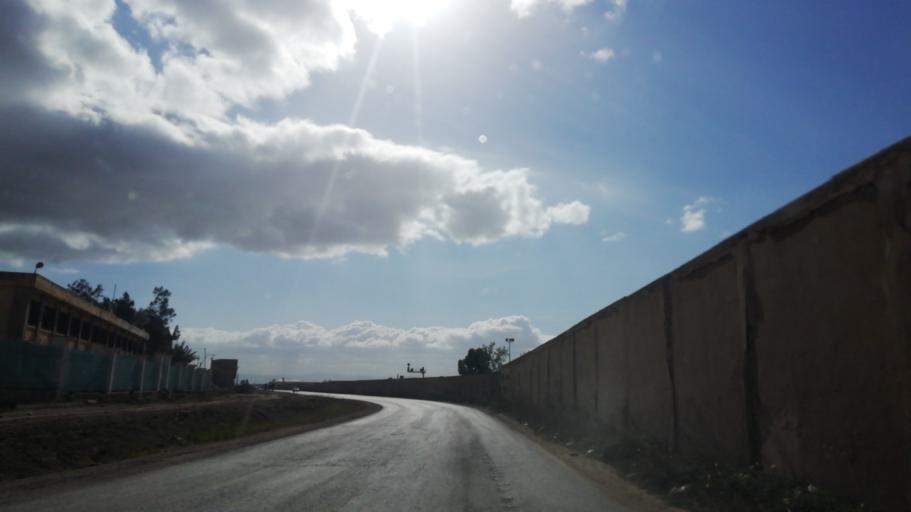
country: DZ
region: Oran
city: Es Senia
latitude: 35.6487
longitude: -0.6060
